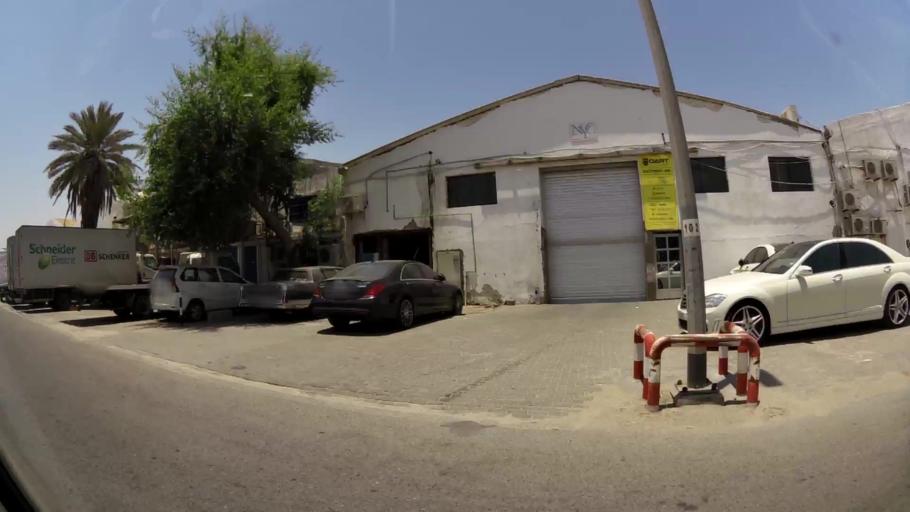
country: AE
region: Ash Shariqah
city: Sharjah
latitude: 25.2654
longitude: 55.3350
